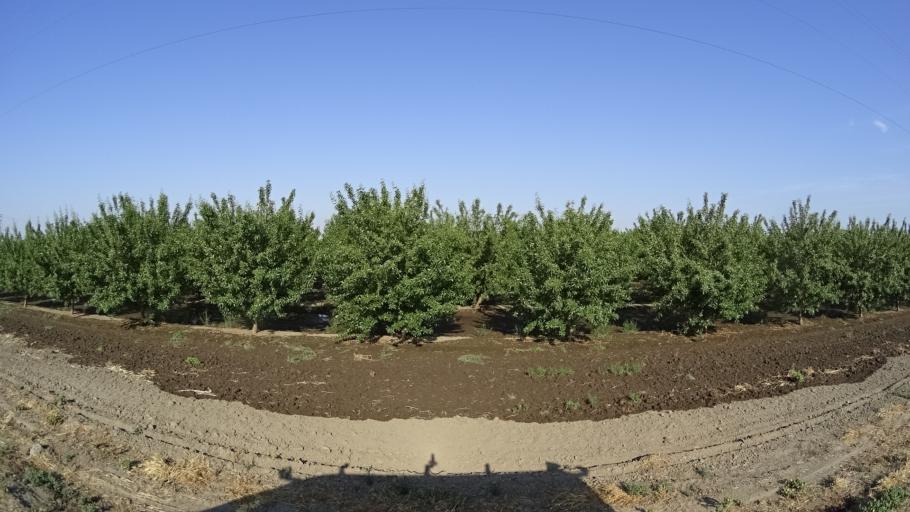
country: US
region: California
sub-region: Fresno County
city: Riverdale
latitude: 36.3815
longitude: -119.8431
